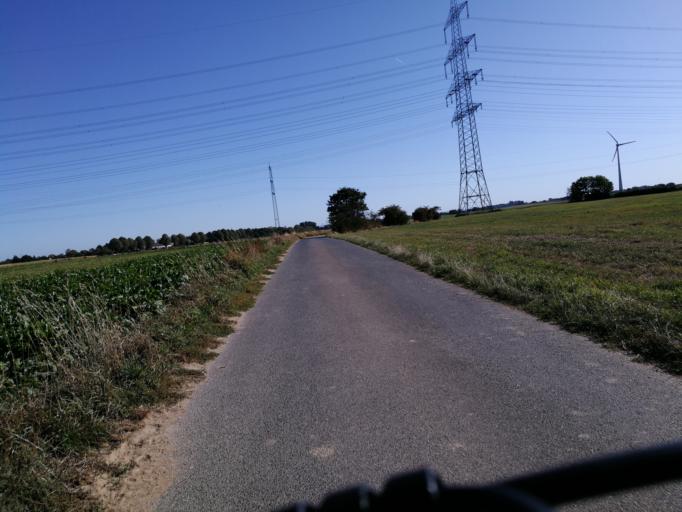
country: DE
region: North Rhine-Westphalia
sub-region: Regierungsbezirk Dusseldorf
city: Neubrueck
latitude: 51.1366
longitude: 6.6871
